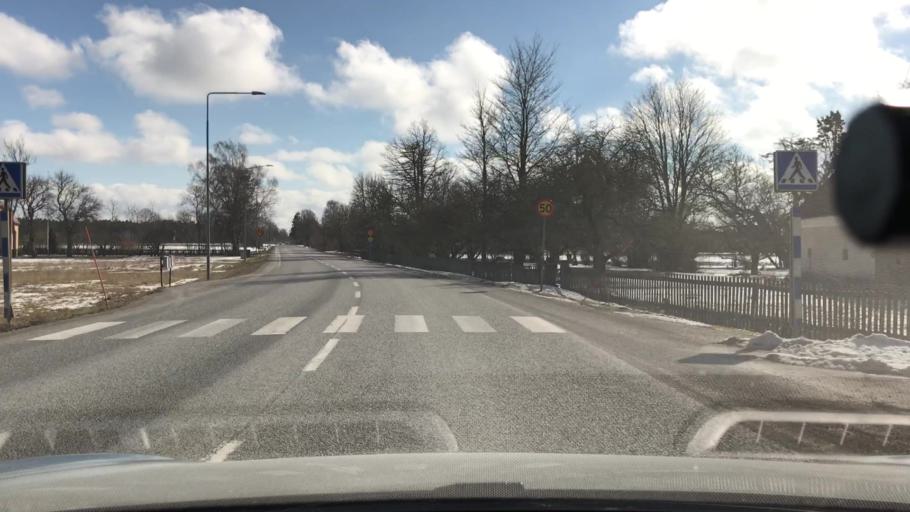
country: SE
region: Gotland
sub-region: Gotland
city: Visby
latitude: 57.5269
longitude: 18.4403
